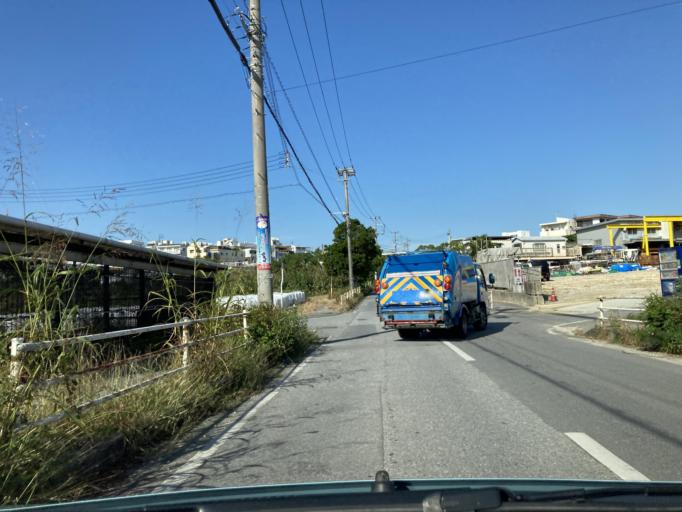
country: JP
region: Okinawa
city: Tomigusuku
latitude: 26.1759
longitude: 127.7056
